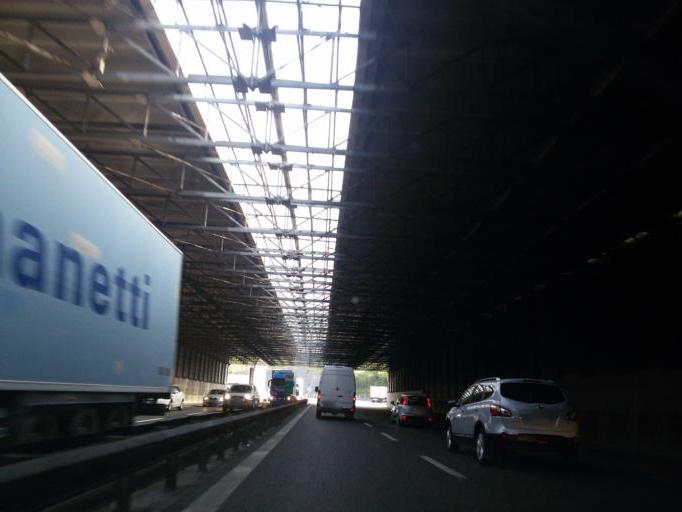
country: IT
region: Liguria
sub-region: Provincia di Genova
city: San Teodoro
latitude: 44.4150
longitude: 8.9017
